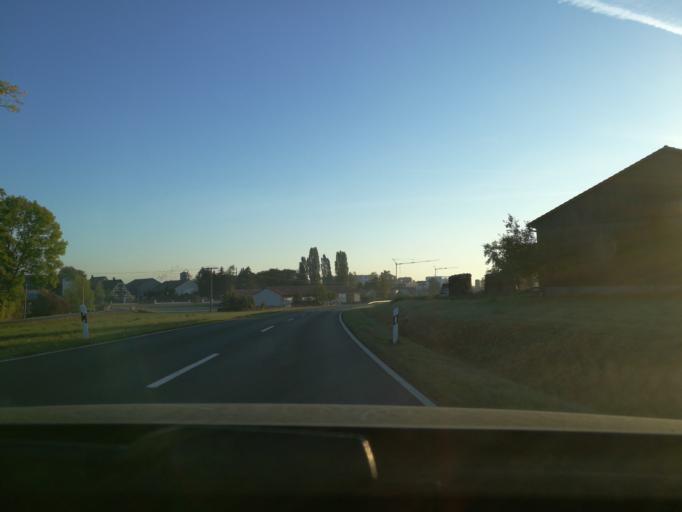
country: DE
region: Bavaria
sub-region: Regierungsbezirk Mittelfranken
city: Obermichelbach
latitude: 49.5292
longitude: 10.9210
